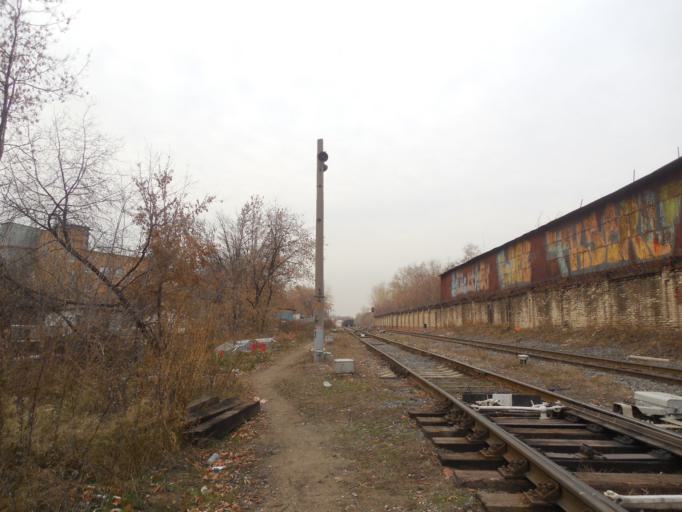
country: RU
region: Moscow
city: Lefortovo
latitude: 55.7417
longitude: 37.7120
